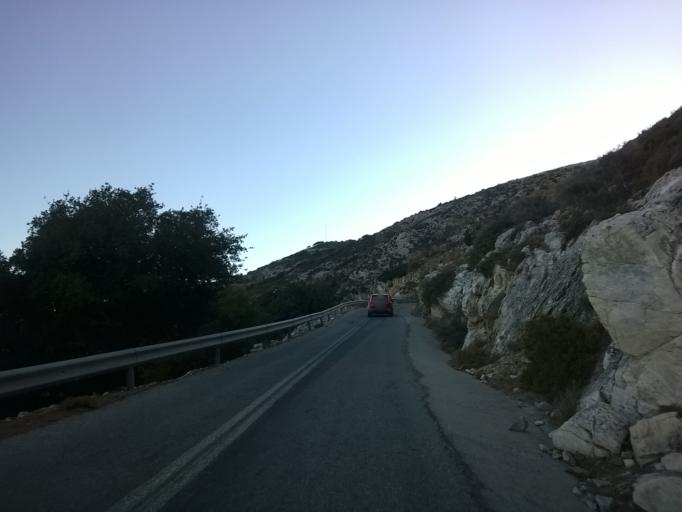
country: GR
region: South Aegean
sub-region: Nomos Kykladon
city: Filotion
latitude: 37.0460
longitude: 25.5046
